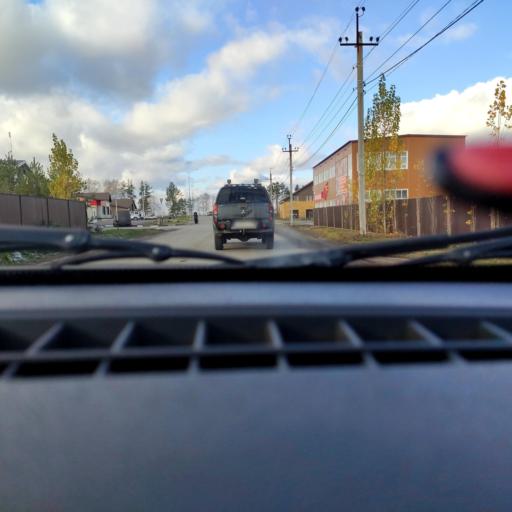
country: RU
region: Bashkortostan
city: Ufa
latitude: 54.6004
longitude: 55.9206
